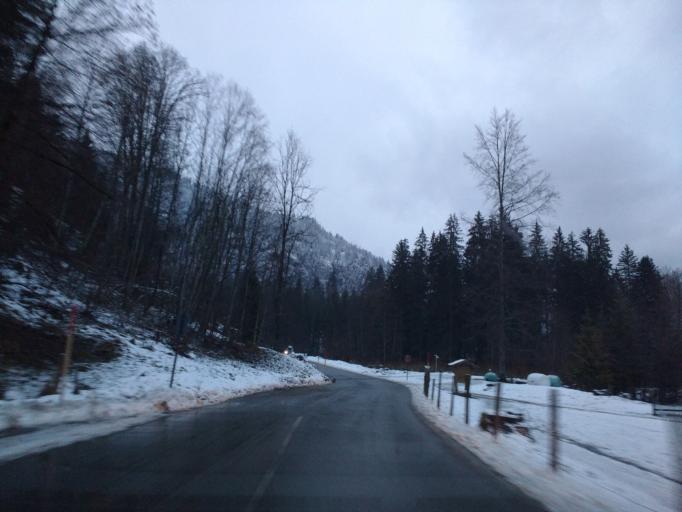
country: DE
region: Bavaria
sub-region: Swabia
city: Obermaiselstein
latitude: 47.4035
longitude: 10.2290
